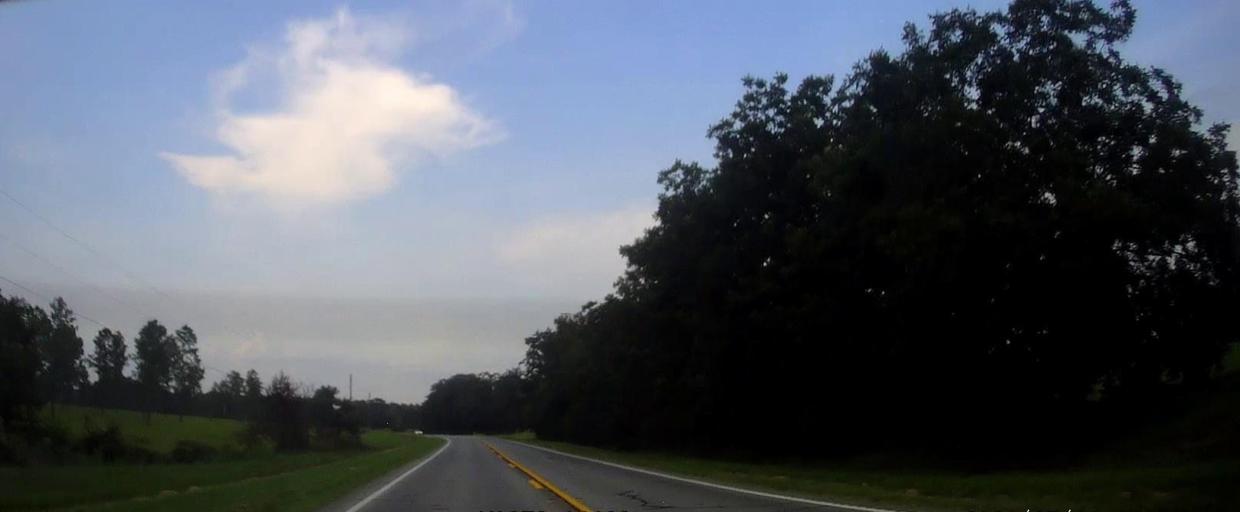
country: US
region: Georgia
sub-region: Laurens County
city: East Dublin
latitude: 32.5940
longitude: -82.8278
